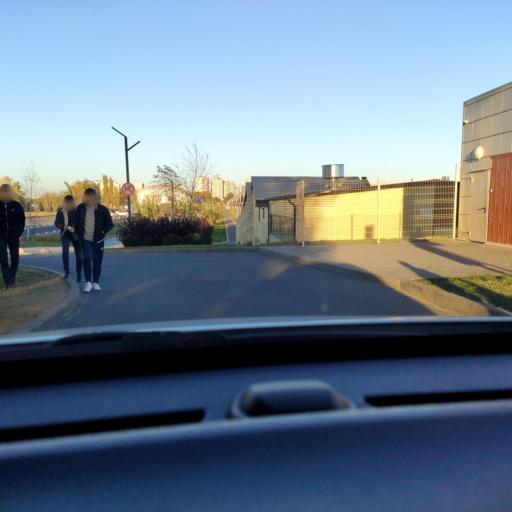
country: RU
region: Voronezj
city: Voronezh
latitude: 51.6699
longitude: 39.2303
